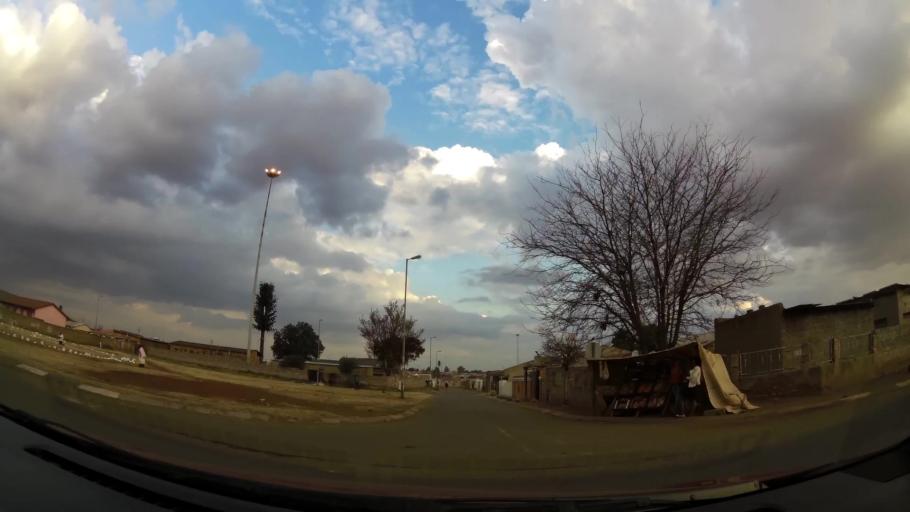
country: ZA
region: Gauteng
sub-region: City of Johannesburg Metropolitan Municipality
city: Soweto
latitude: -26.2468
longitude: 27.8248
